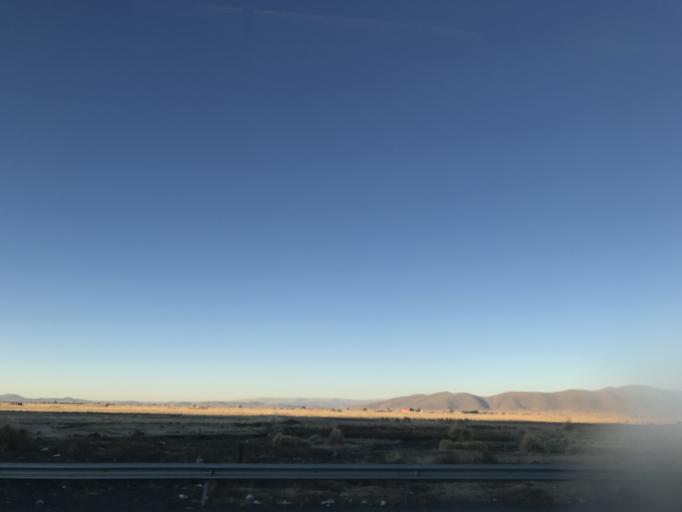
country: BO
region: La Paz
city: Batallas
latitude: -16.2988
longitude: -68.5182
